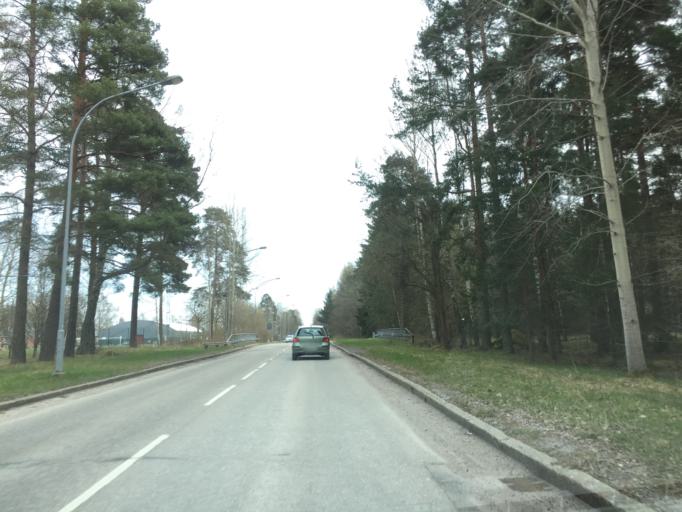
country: SE
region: OErebro
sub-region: Orebro Kommun
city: Orebro
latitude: 59.2953
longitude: 15.1843
